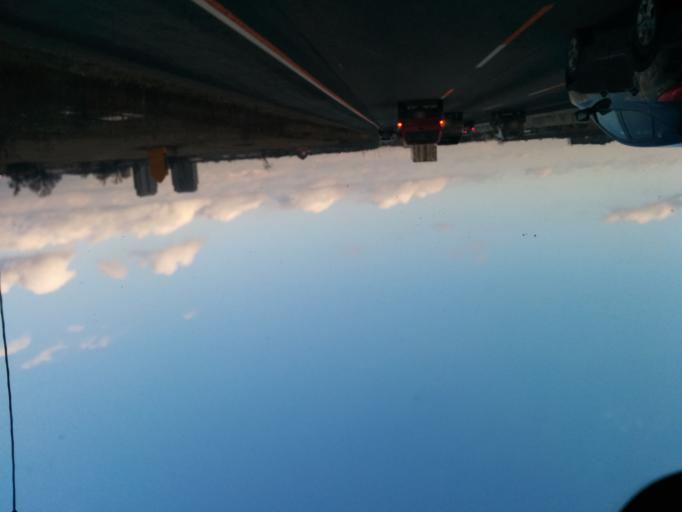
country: CA
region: Ontario
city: Etobicoke
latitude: 43.7106
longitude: -79.6153
